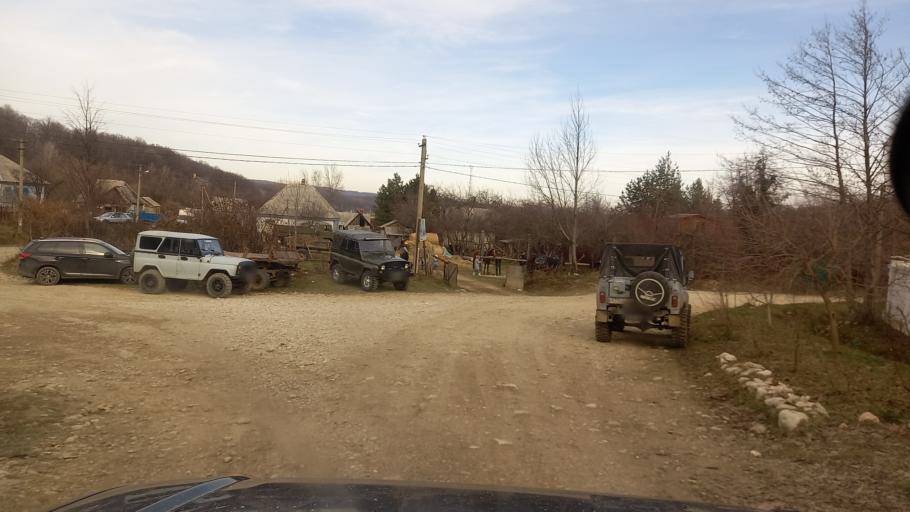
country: RU
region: Krasnodarskiy
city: Neftegorsk
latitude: 44.2267
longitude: 39.9018
